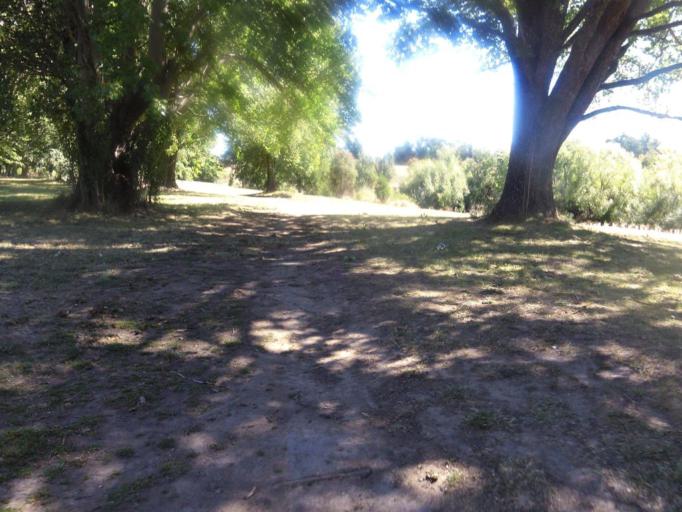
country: AU
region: Victoria
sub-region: Mount Alexander
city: Castlemaine
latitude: -37.2402
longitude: 144.4418
